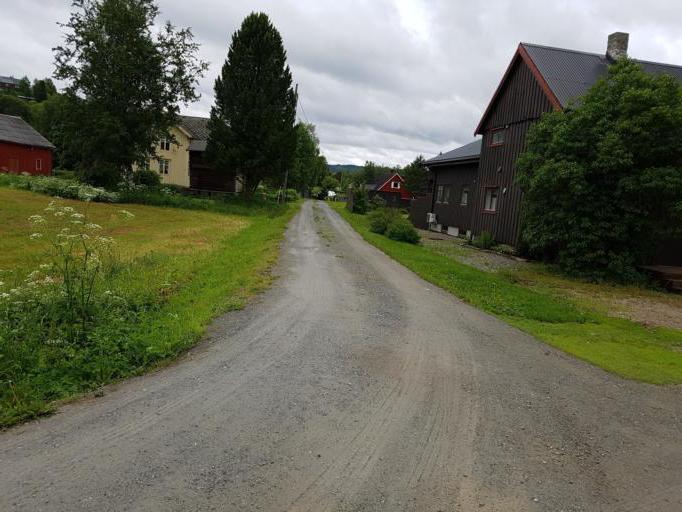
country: NO
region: Sor-Trondelag
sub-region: Selbu
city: Mebonden
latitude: 63.2321
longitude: 11.0318
